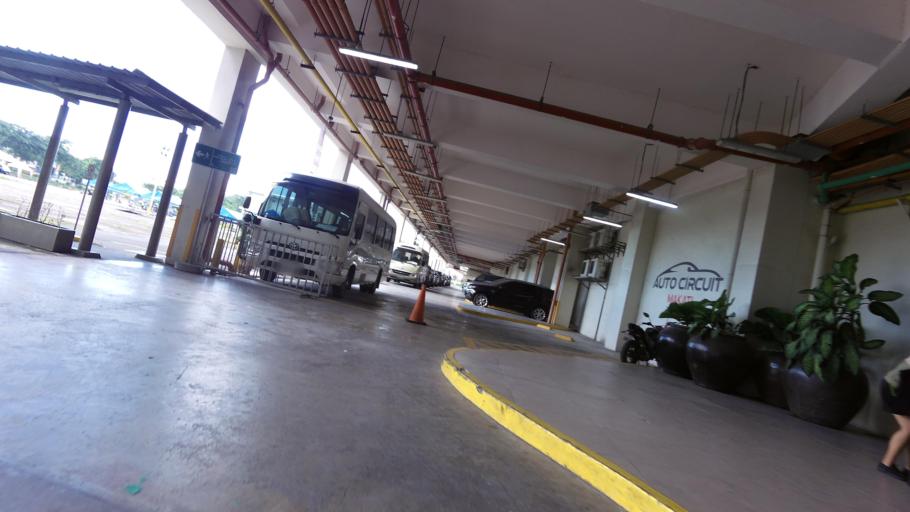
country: PH
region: Metro Manila
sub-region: Mandaluyong
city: Mandaluyong City
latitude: 14.5753
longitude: 121.0195
